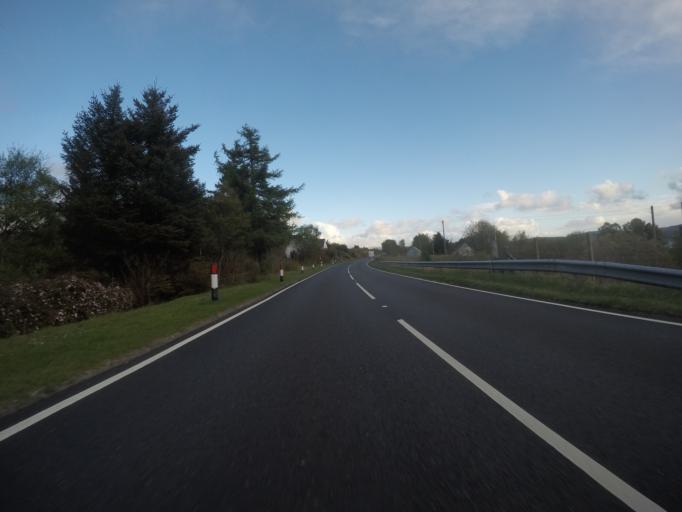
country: GB
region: Scotland
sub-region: Highland
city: Portree
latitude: 57.4986
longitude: -6.3238
